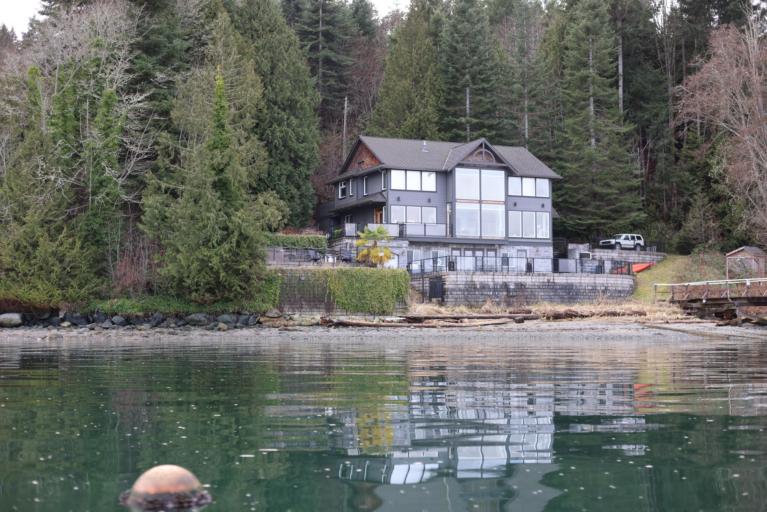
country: CA
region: British Columbia
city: Duncan
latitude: 48.7261
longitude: -123.5704
